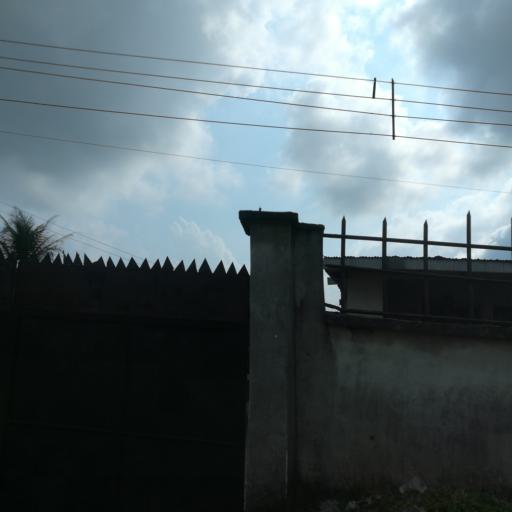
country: NG
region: Rivers
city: Okrika
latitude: 4.7964
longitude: 7.1229
